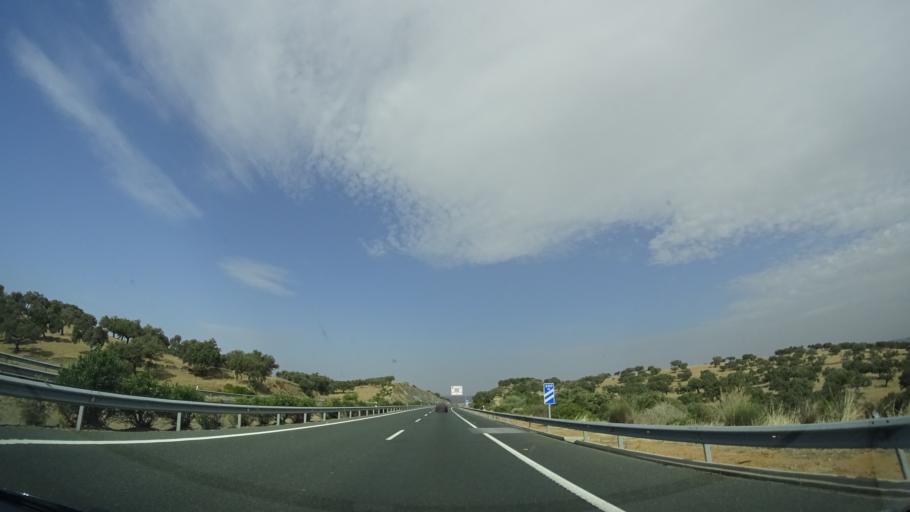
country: ES
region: Extremadura
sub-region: Provincia de Badajoz
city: Monesterio
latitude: 38.1278
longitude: -6.2719
